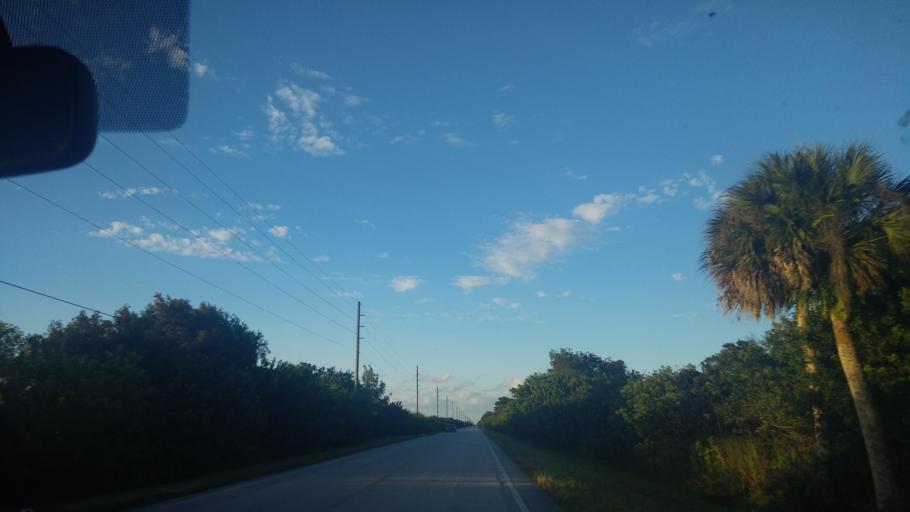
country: US
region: Florida
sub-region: Indian River County
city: Fellsmere
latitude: 27.6649
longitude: -80.6432
